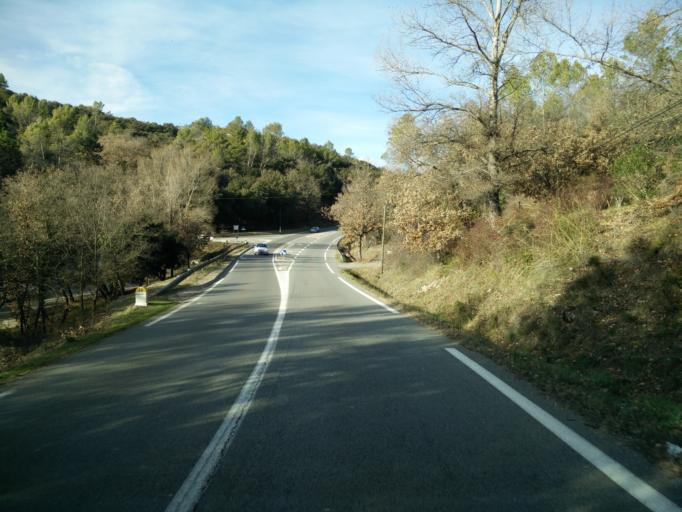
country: FR
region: Provence-Alpes-Cote d'Azur
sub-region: Departement du Var
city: Montauroux
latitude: 43.5887
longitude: 6.7905
